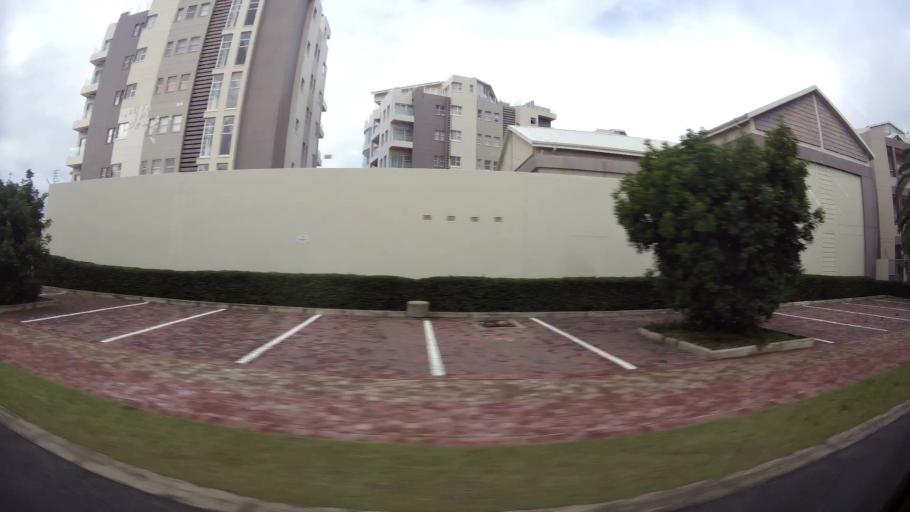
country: ZA
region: Western Cape
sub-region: Eden District Municipality
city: Mossel Bay
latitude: -34.1617
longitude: 22.1093
